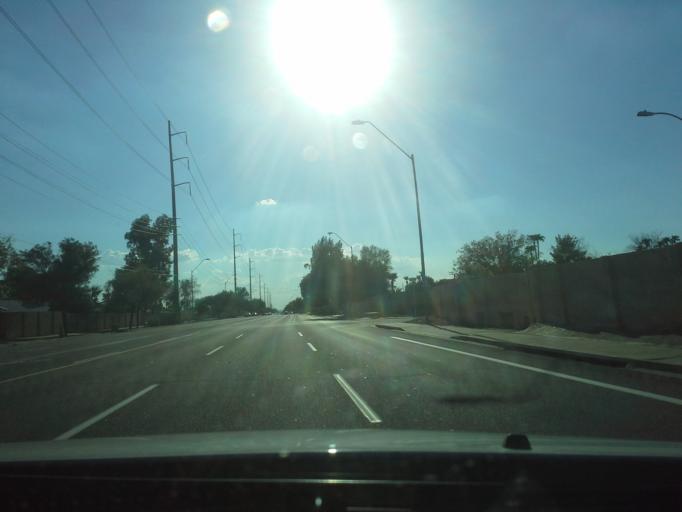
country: US
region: Arizona
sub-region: Maricopa County
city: Glendale
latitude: 33.6547
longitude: -112.1210
